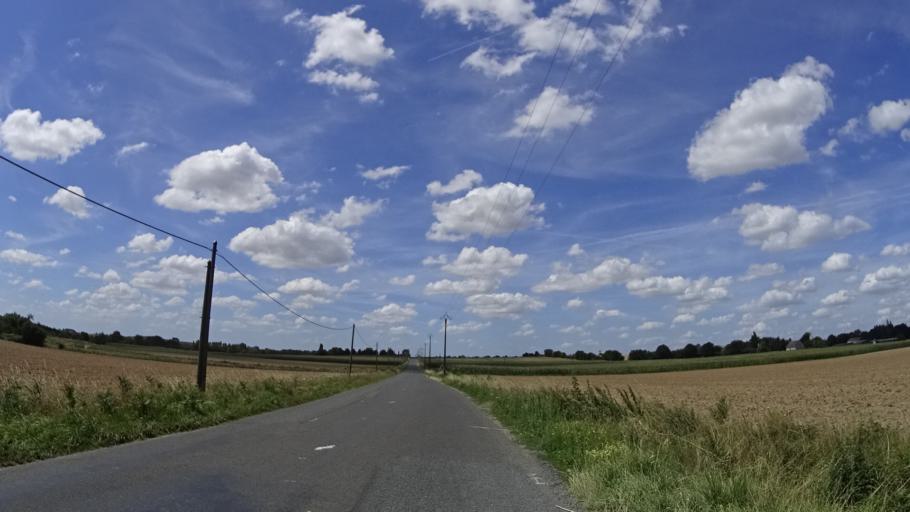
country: FR
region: Pays de la Loire
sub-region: Departement de Maine-et-Loire
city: Segre
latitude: 47.6124
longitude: -0.9193
